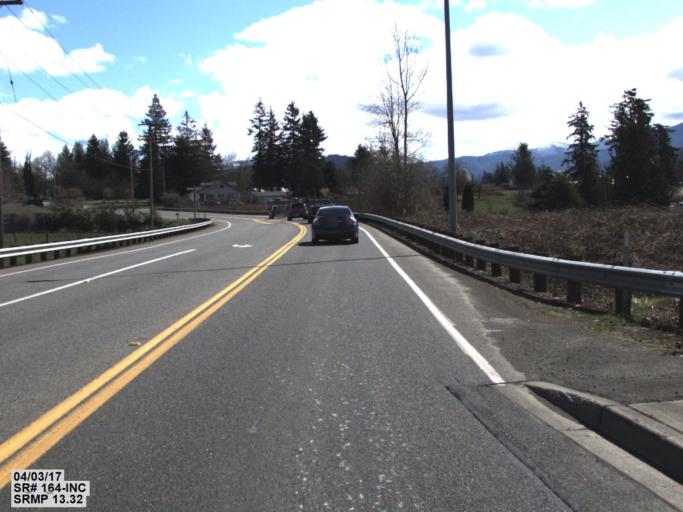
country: US
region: Washington
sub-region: King County
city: Enumclaw
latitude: 47.2073
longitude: -122.0159
